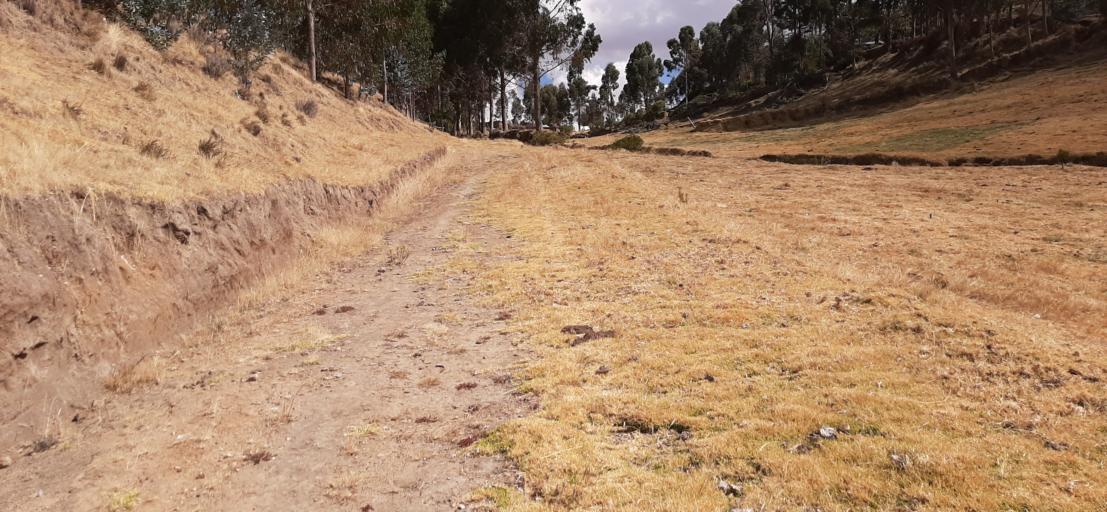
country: PE
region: Cusco
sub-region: Provincia de Chumbivilcas
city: Chamaca
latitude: -14.2572
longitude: -71.8783
